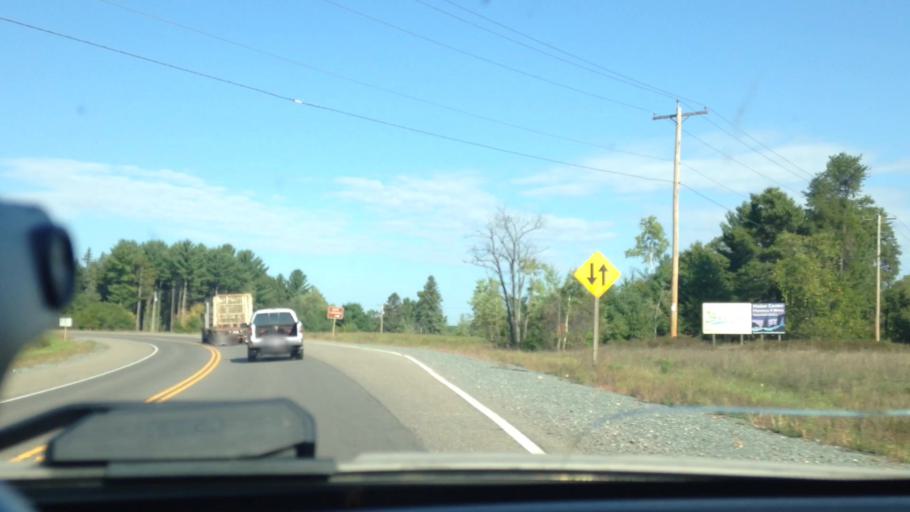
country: US
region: Michigan
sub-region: Dickinson County
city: Iron Mountain
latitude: 45.8747
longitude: -88.0856
